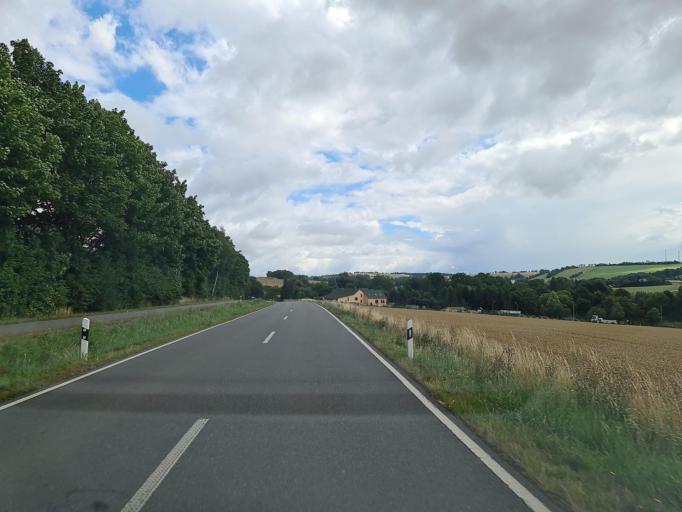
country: DE
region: Saxony
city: Eppendorf
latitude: 50.7922
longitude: 13.2554
